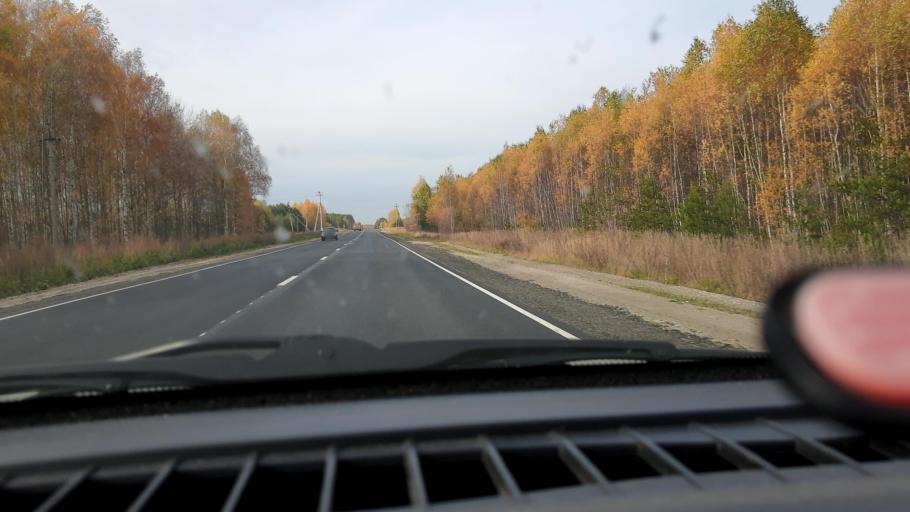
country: RU
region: Nizjnij Novgorod
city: Novaya Balakhna
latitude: 56.6011
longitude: 43.6317
